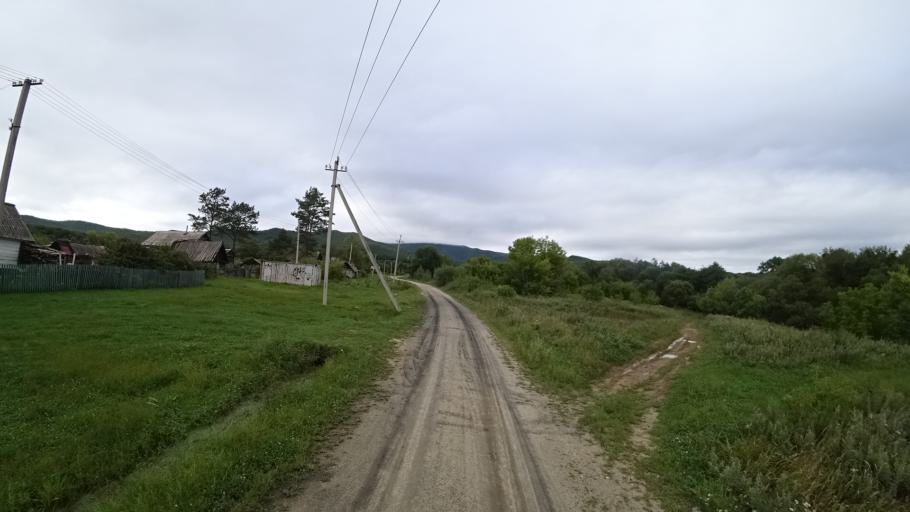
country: RU
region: Primorskiy
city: Rettikhovka
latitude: 44.1386
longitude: 132.6425
